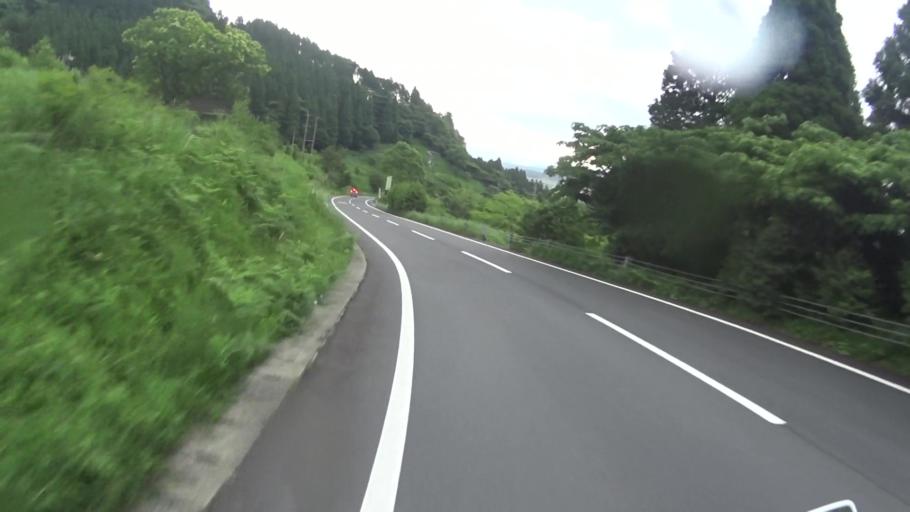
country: JP
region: Kumamoto
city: Aso
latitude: 32.9151
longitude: 130.9719
